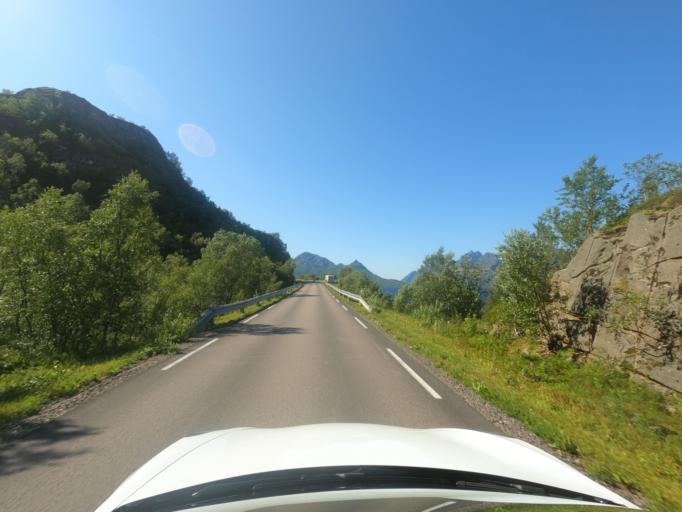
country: NO
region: Nordland
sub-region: Hadsel
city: Stokmarknes
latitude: 68.3272
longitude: 15.0115
